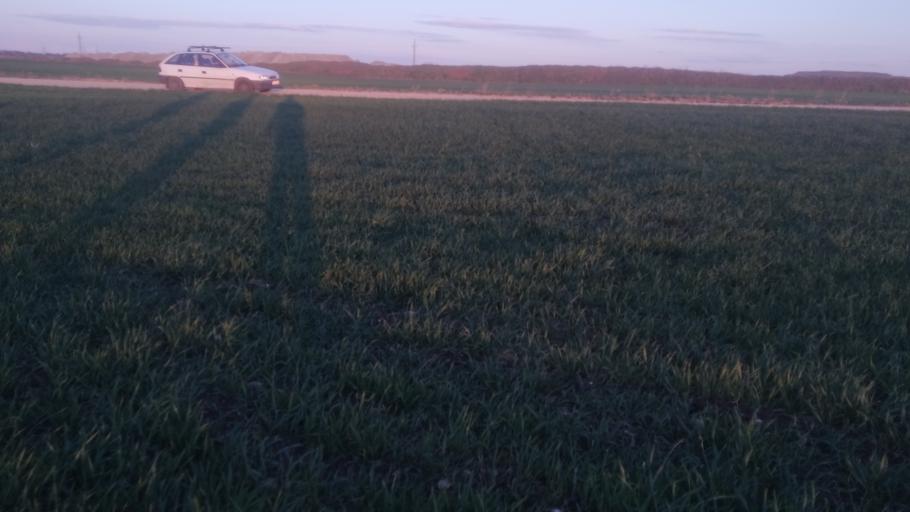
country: HU
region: Veszprem
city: Osi
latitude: 47.1948
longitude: 18.1885
